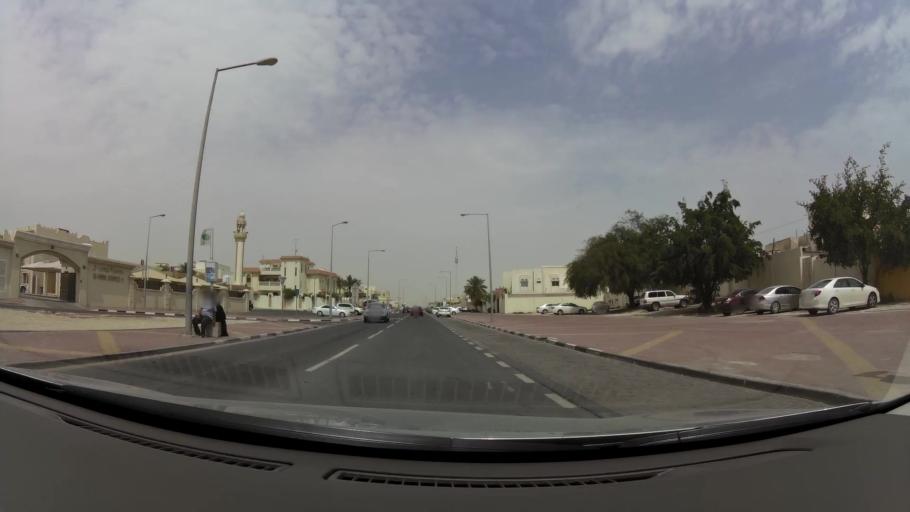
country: QA
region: Baladiyat ad Dawhah
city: Doha
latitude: 25.3150
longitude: 51.4786
